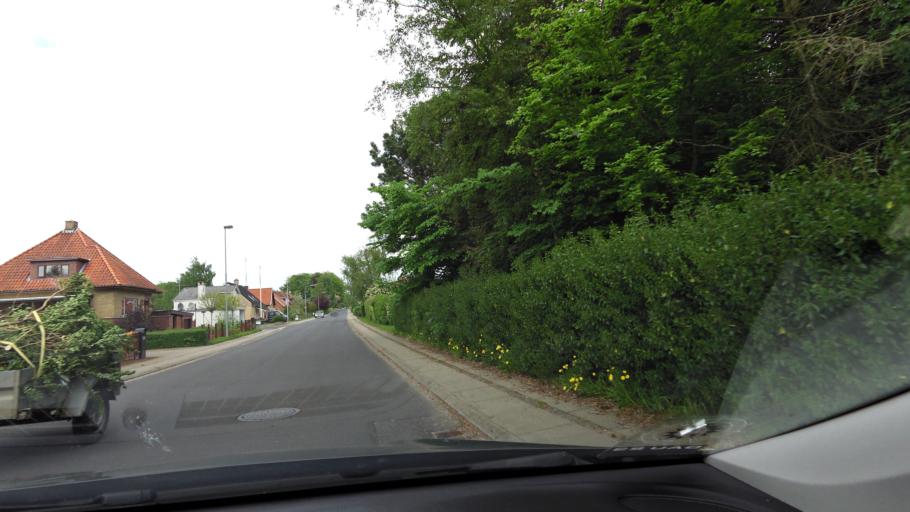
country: DK
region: South Denmark
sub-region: Svendborg Kommune
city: Thuro By
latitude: 55.1712
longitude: 10.7377
